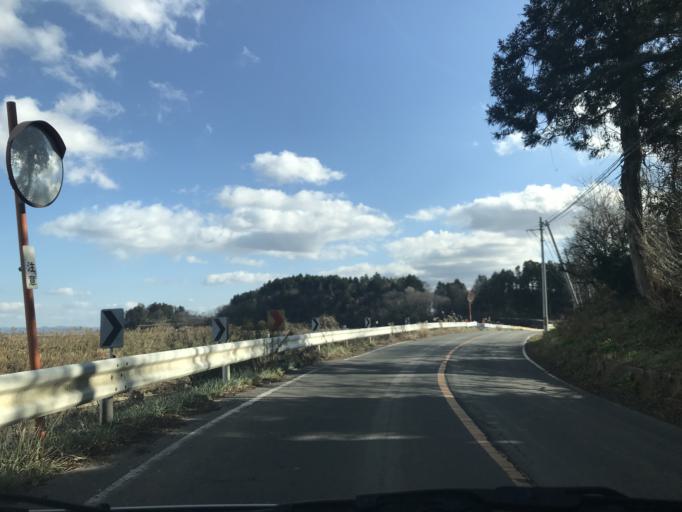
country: JP
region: Miyagi
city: Kogota
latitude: 38.7208
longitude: 141.0691
